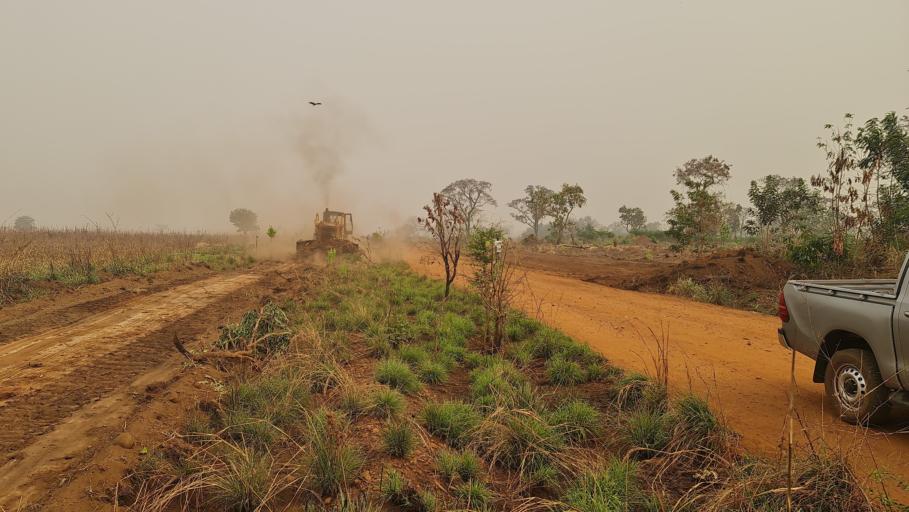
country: ET
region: Gambela
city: Gambela
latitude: 7.6363
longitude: 34.2753
